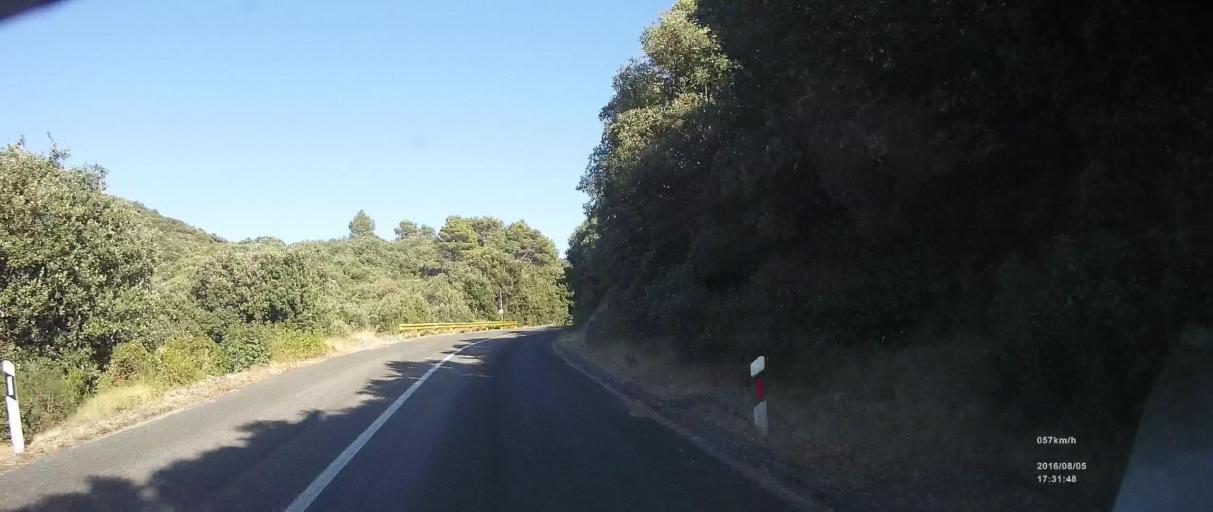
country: HR
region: Dubrovacko-Neretvanska
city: Blato
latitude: 42.7723
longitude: 17.4239
